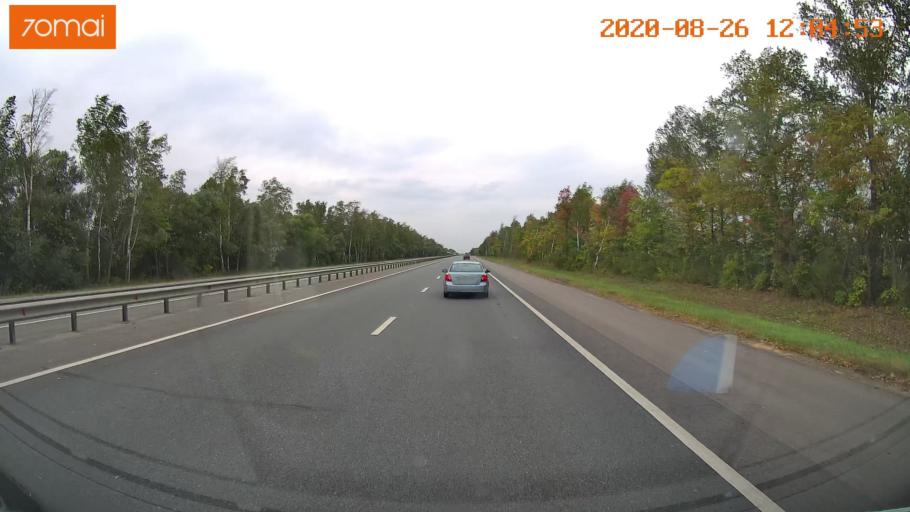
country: RU
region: Rjazan
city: Kiritsy
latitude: 54.3152
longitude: 40.1787
